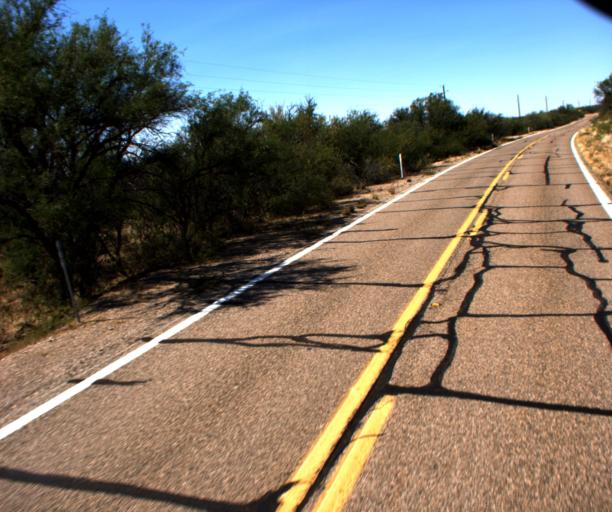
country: US
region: Arizona
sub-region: Pima County
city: Three Points
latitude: 31.8619
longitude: -111.3986
